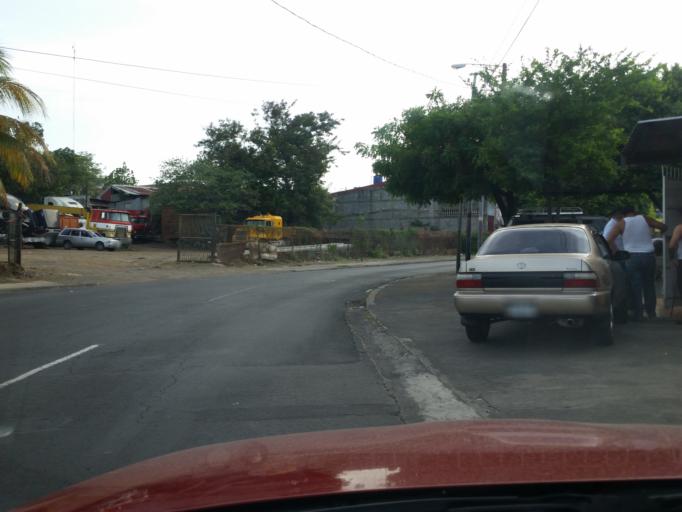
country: NI
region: Managua
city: Managua
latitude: 12.1459
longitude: -86.2757
